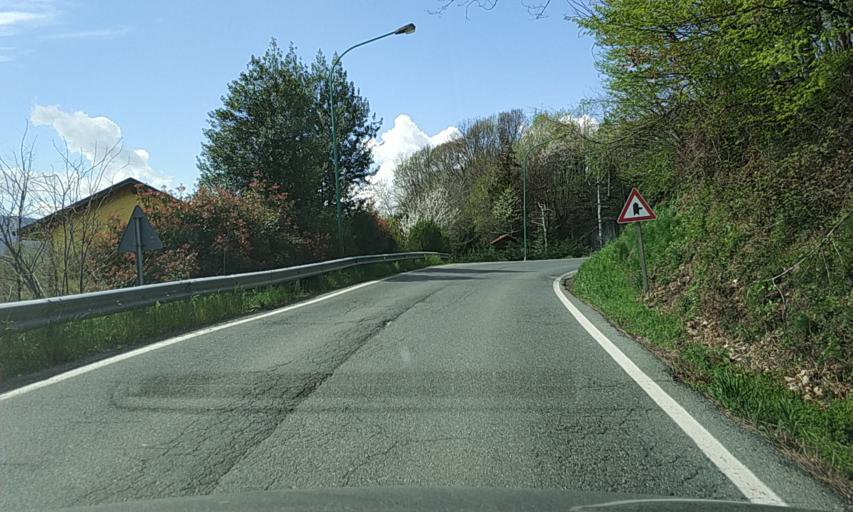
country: IT
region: Piedmont
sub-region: Provincia di Torino
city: San Carlo Canavese
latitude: 45.2474
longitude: 7.5977
